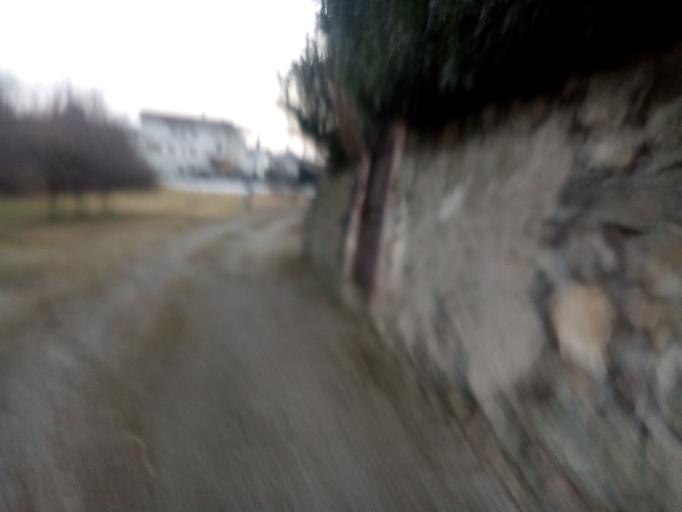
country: IT
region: Piedmont
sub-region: Provincia di Torino
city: Cascinette d'Ivrea
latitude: 45.4867
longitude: 7.9056
